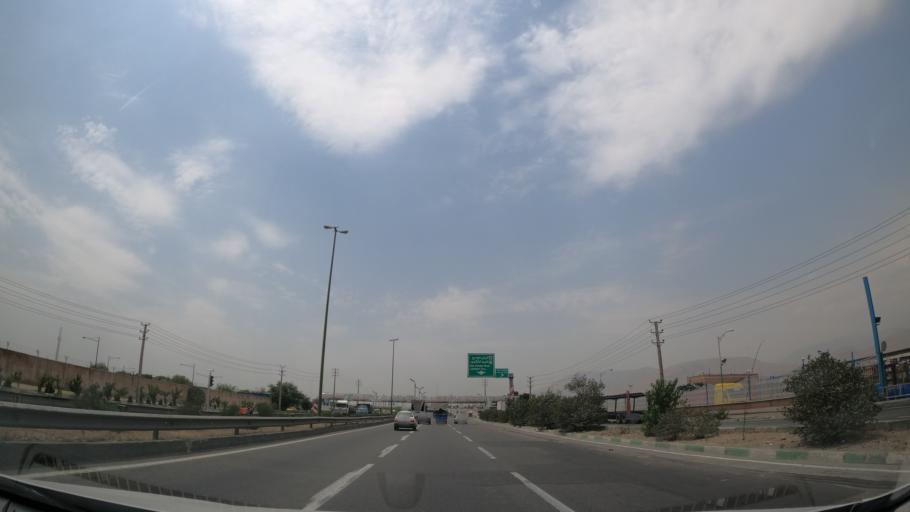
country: IR
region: Tehran
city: Shahr-e Qods
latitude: 35.7017
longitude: 51.1880
